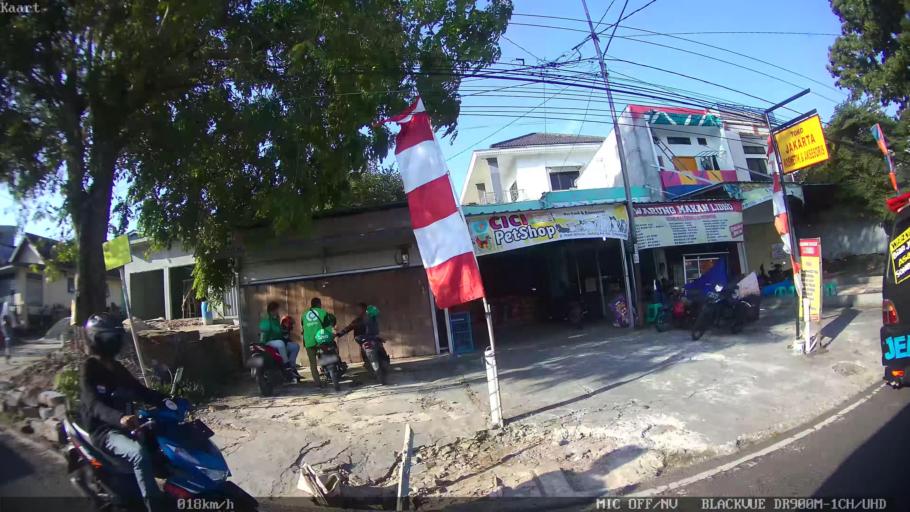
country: ID
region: Lampung
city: Kedaton
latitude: -5.4003
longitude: 105.2464
